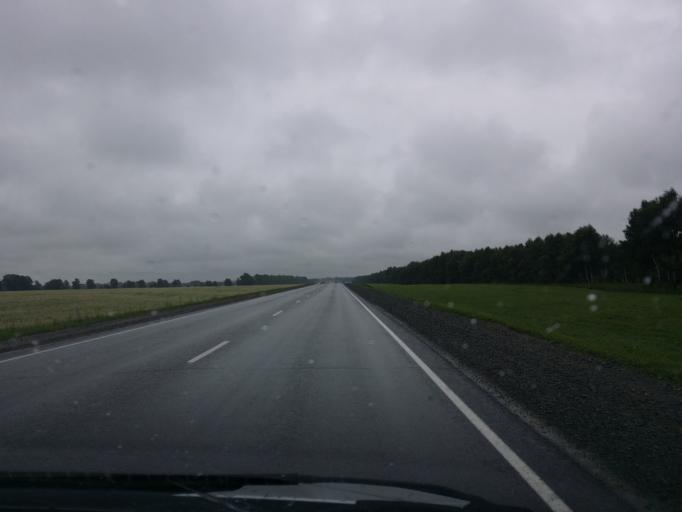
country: RU
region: Altai Krai
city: Bayunovskiye Klyuchi
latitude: 53.2960
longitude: 84.2904
